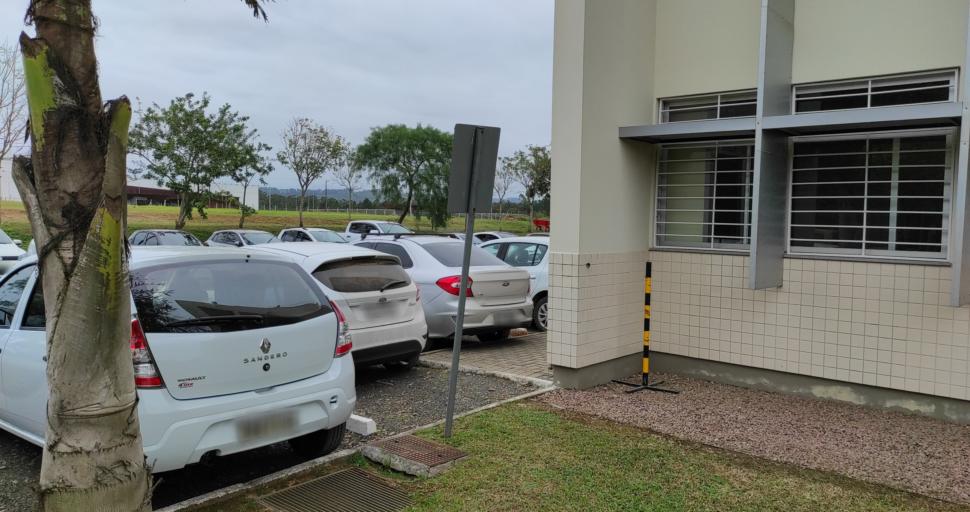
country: BR
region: Santa Catarina
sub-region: Criciuma
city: Criciuma
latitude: -28.7076
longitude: -49.4140
